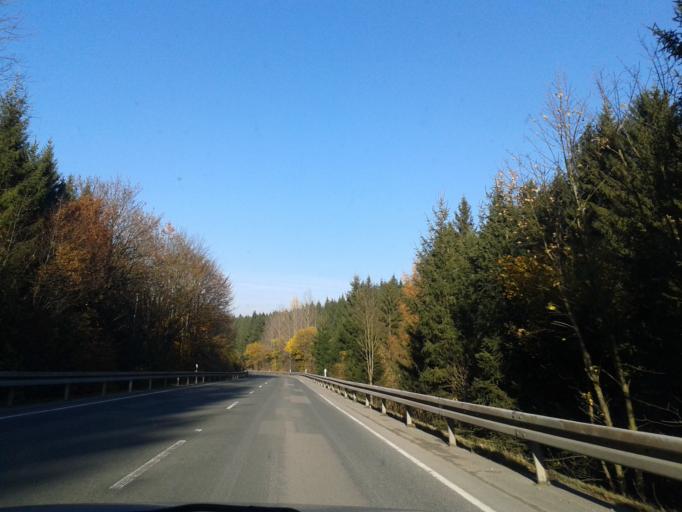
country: DE
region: North Rhine-Westphalia
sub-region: Regierungsbezirk Arnsberg
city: Bestwig
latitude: 51.4091
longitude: 8.4169
